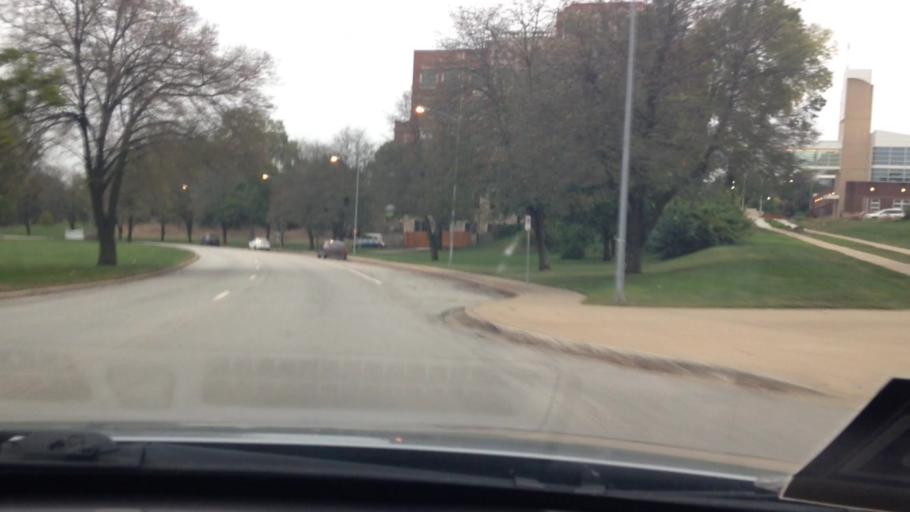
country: US
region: Kansas
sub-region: Johnson County
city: Westwood
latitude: 39.0582
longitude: -94.5825
